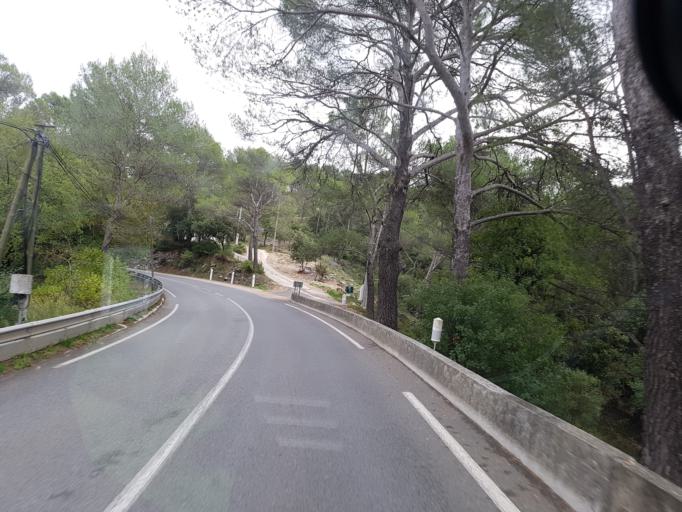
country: FR
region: Provence-Alpes-Cote d'Azur
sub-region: Departement des Bouches-du-Rhone
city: Cuges-les-Pins
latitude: 43.2663
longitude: 5.7289
